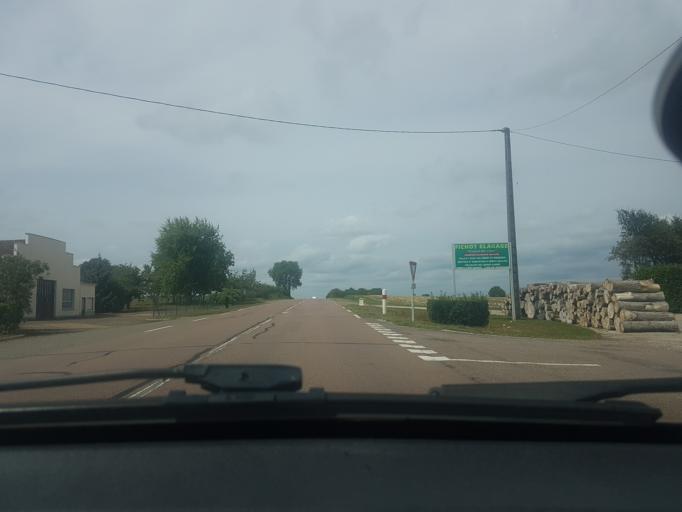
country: FR
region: Bourgogne
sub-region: Departement de la Cote-d'Or
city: Nolay
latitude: 47.0333
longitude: 4.6367
